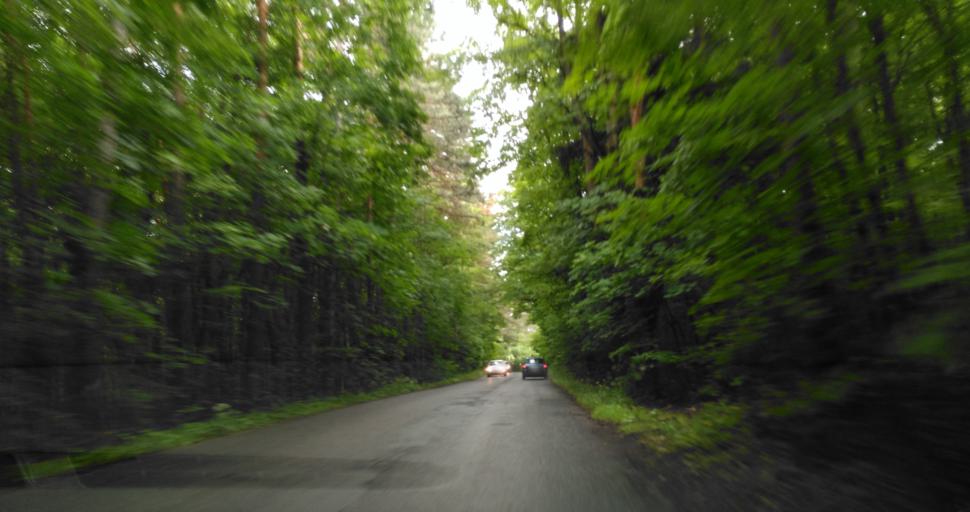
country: CZ
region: Central Bohemia
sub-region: Okres Beroun
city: Beroun
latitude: 49.9027
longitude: 14.0777
